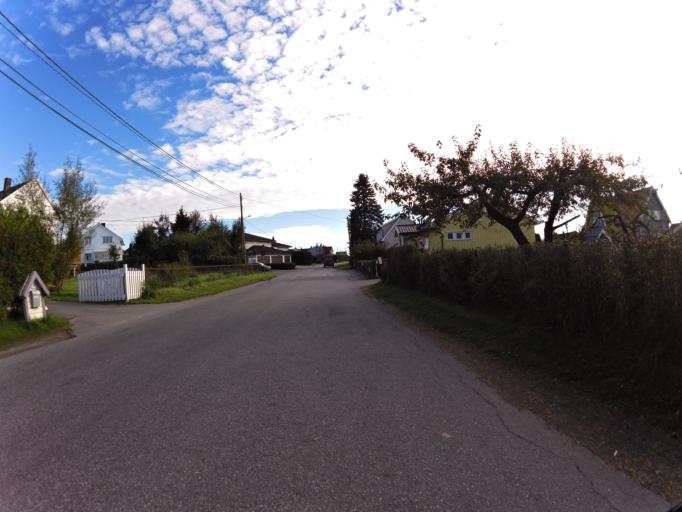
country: NO
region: Ostfold
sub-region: Sarpsborg
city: Sarpsborg
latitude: 59.2839
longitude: 11.0833
